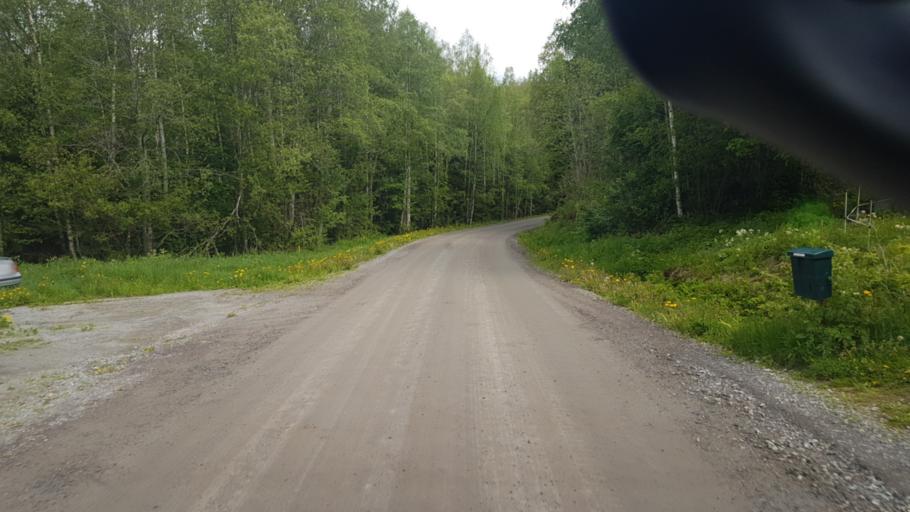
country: NO
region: Ostfold
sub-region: Romskog
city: Romskog
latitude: 59.6966
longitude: 11.9446
